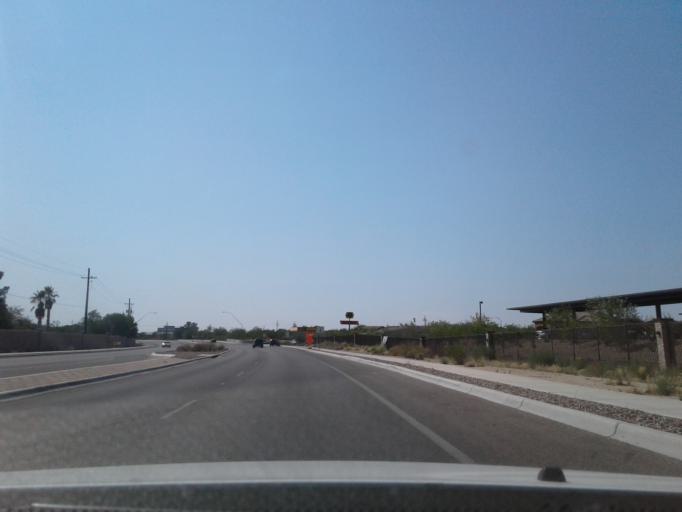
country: US
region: Arizona
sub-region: Pima County
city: Casas Adobes
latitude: 32.3568
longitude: -111.0352
